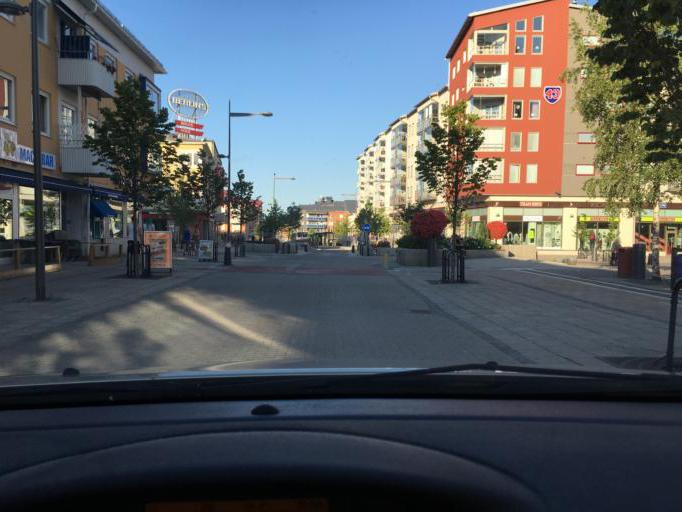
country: SE
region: Norrbotten
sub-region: Bodens Kommun
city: Boden
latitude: 65.8251
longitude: 21.6879
